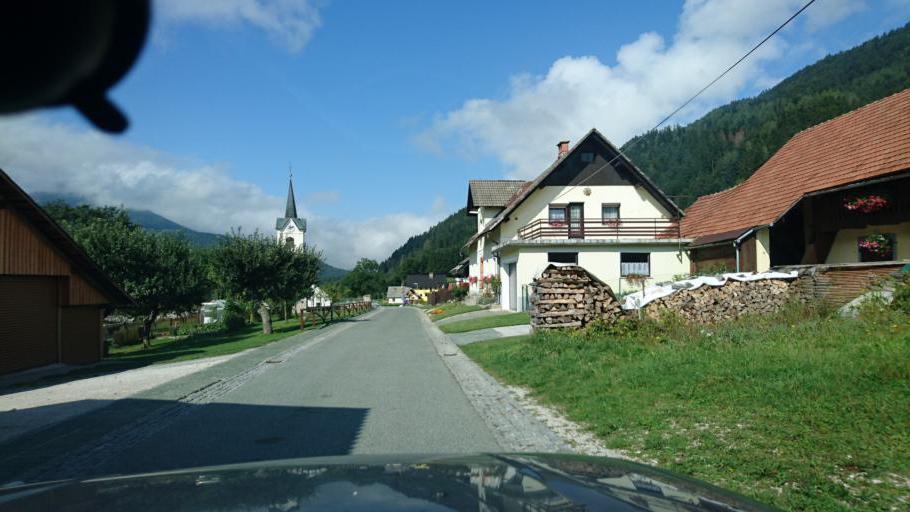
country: SI
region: Kranjska Gora
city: Kranjska Gora
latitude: 46.4937
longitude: 13.7553
